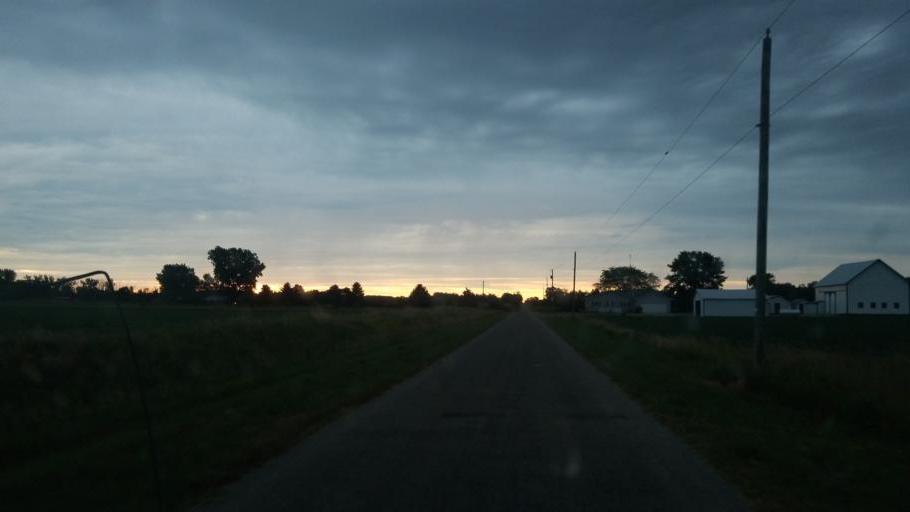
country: US
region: Ohio
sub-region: Defiance County
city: Hicksville
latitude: 41.3681
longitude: -84.7827
